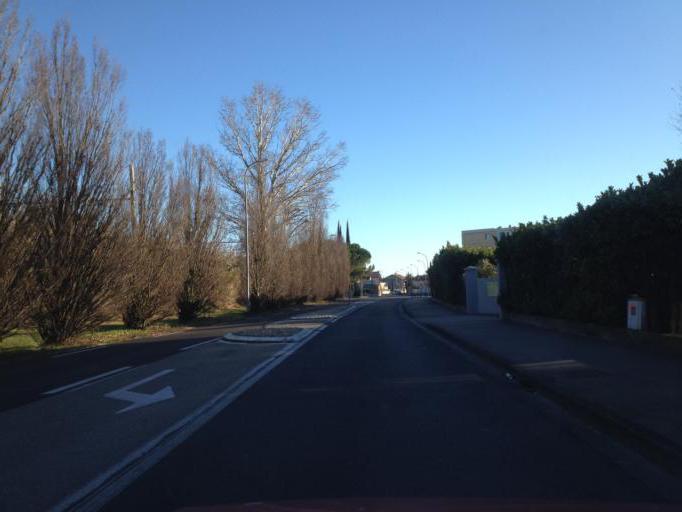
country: FR
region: Provence-Alpes-Cote d'Azur
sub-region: Departement du Vaucluse
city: Orange
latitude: 44.1430
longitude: 4.8125
